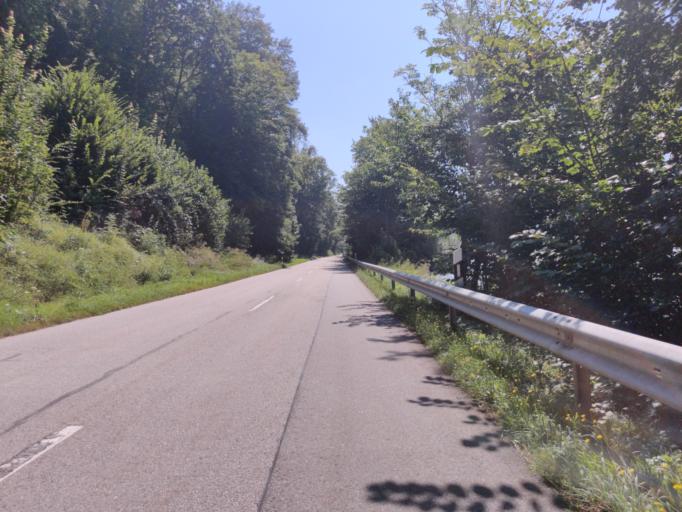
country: DE
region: Bavaria
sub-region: Lower Bavaria
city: Untergriesbach
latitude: 48.5271
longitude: 13.6919
